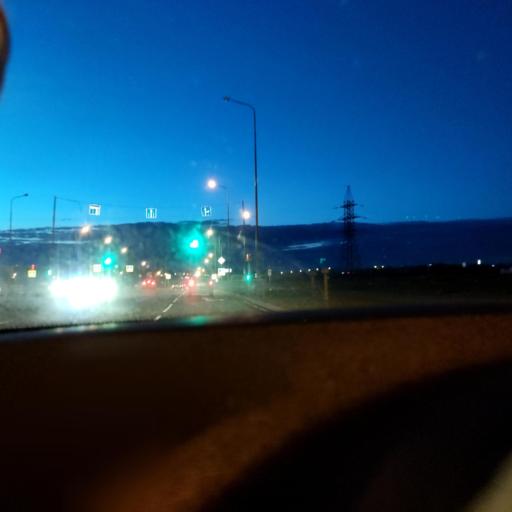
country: RU
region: Samara
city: Petra-Dubrava
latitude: 53.2981
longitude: 50.3210
